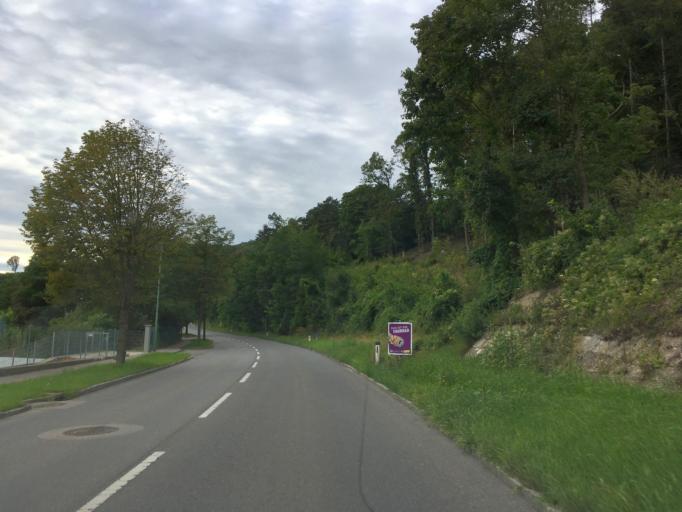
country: AT
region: Lower Austria
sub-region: Politischer Bezirk Tulln
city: Wordern
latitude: 48.3161
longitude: 16.2394
